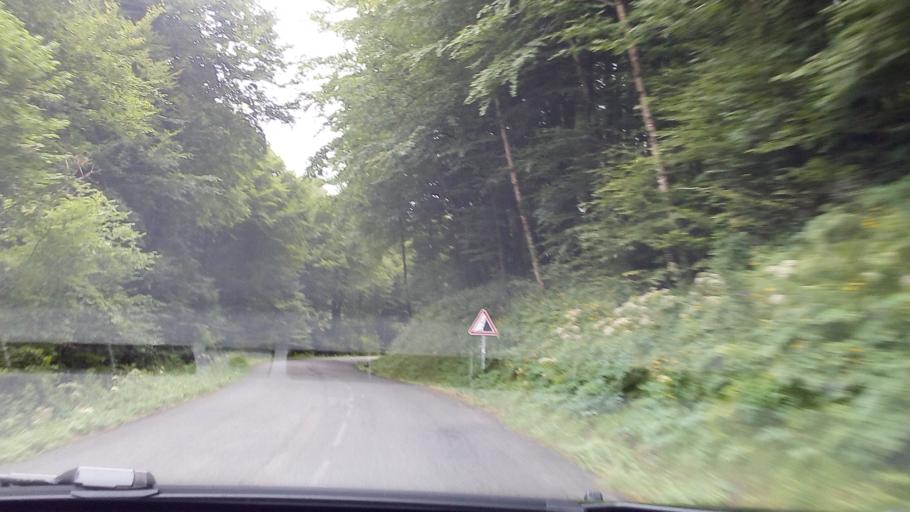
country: FR
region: Aquitaine
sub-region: Departement des Pyrenees-Atlantiques
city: Ogeu-les-Bains
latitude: 43.0706
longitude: -0.5144
